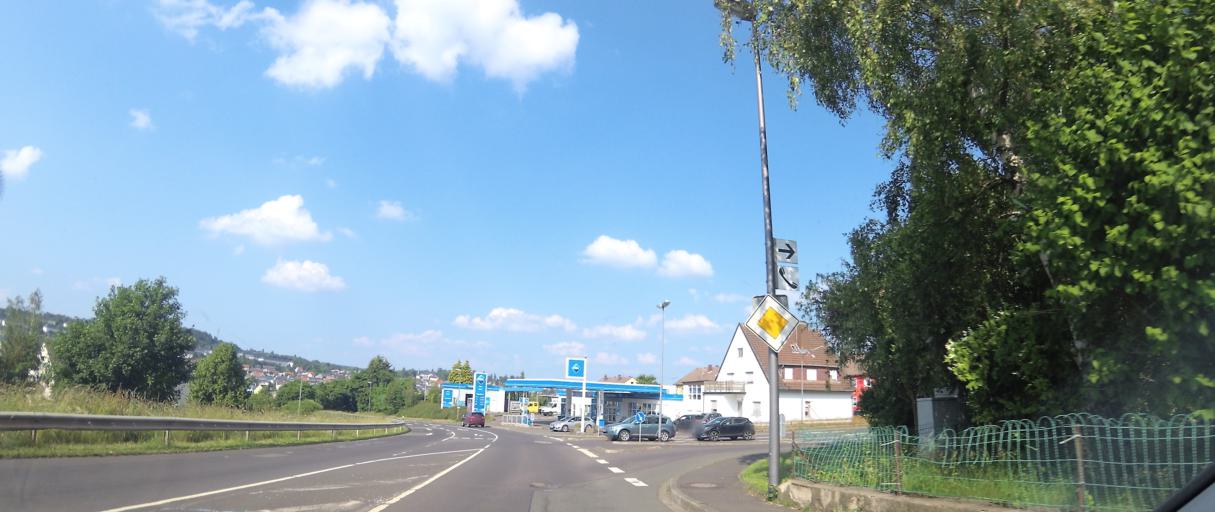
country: DE
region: Rheinland-Pfalz
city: Baumholder
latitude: 49.6090
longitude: 7.3281
